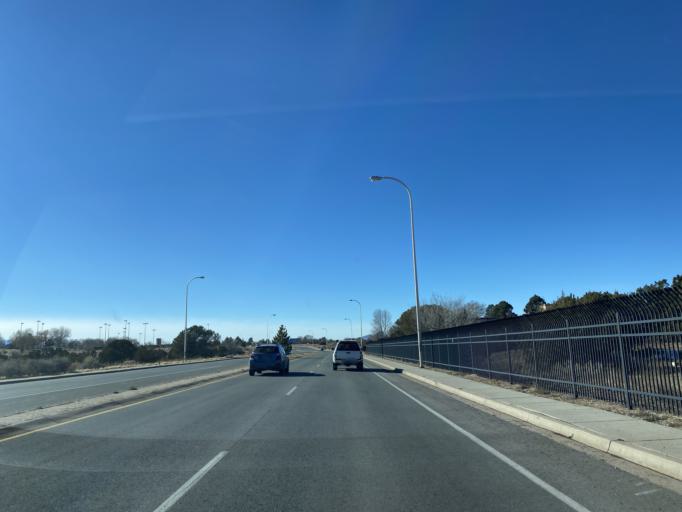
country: US
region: New Mexico
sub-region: Santa Fe County
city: Santa Fe
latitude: 35.6453
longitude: -105.9676
